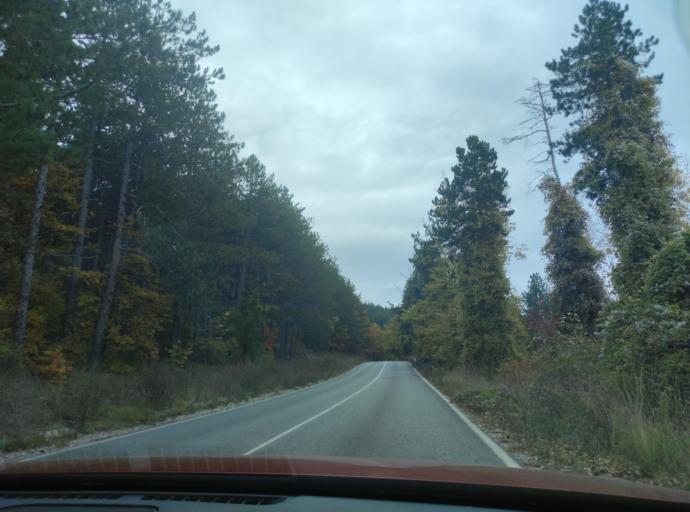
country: BG
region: Sofiya
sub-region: Obshtina Godech
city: Godech
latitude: 43.0135
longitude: 23.1204
